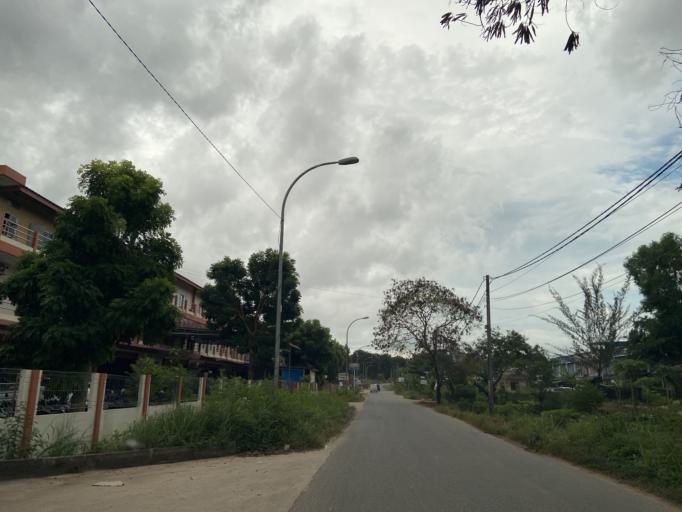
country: SG
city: Singapore
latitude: 1.1112
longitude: 104.0494
